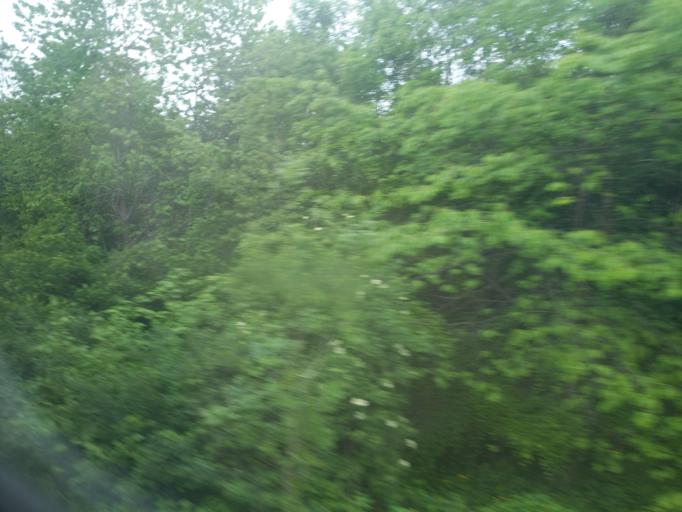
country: GB
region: England
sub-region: Devon
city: Winkleigh
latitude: 50.8955
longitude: -3.8775
